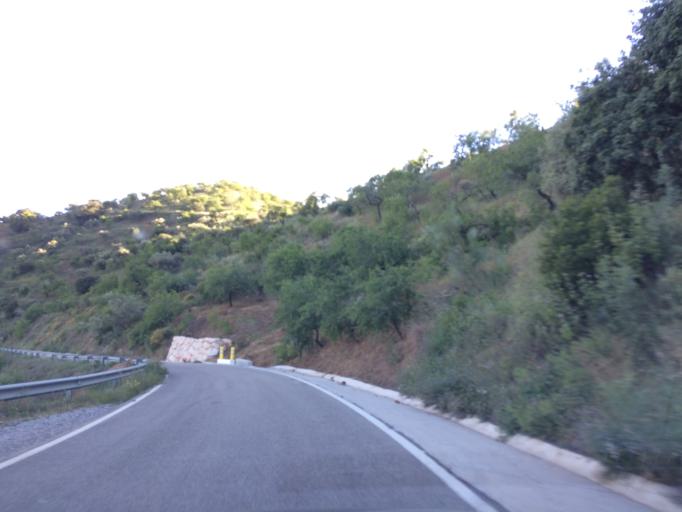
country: ES
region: Andalusia
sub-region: Provincia de Malaga
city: Totalan
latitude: 36.7826
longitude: -4.3211
